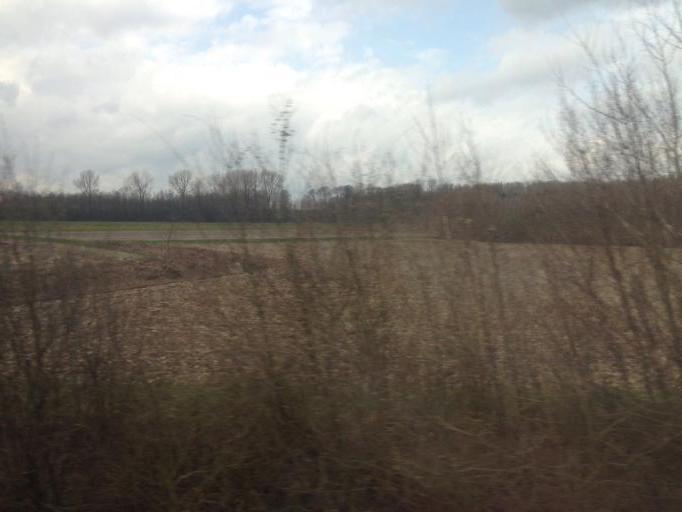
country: DE
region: North Rhine-Westphalia
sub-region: Regierungsbezirk Munster
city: Dulmen
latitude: 51.8519
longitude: 7.3425
